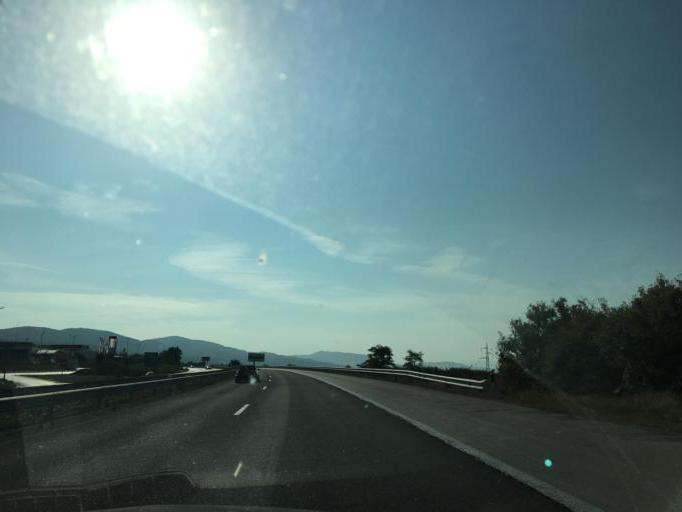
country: BG
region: Sofiya
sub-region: Obshtina Ikhtiman
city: Ikhtiman
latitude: 42.4783
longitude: 23.7960
